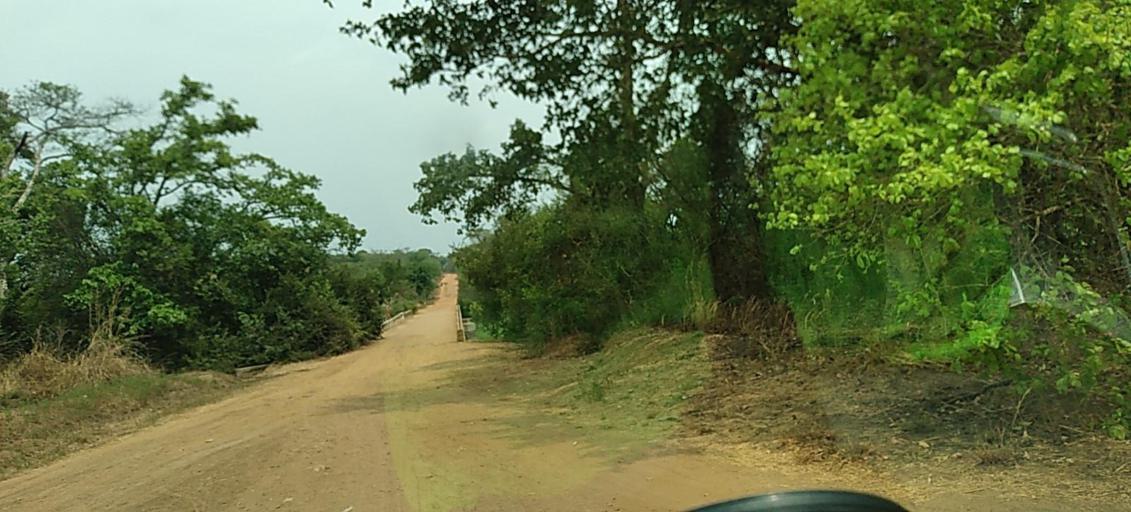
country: ZM
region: North-Western
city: Solwezi
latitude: -12.7954
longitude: 26.5326
